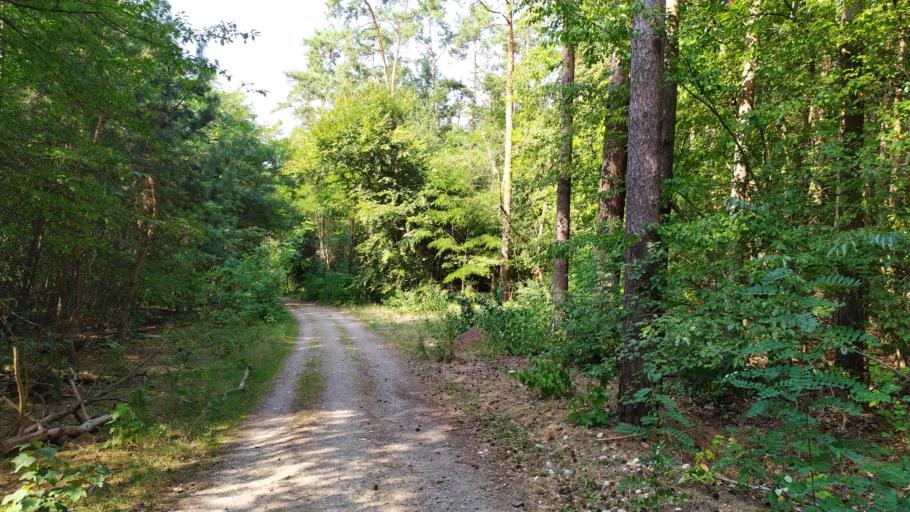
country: DE
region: Berlin
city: Grunau
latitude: 52.4142
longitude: 13.6067
